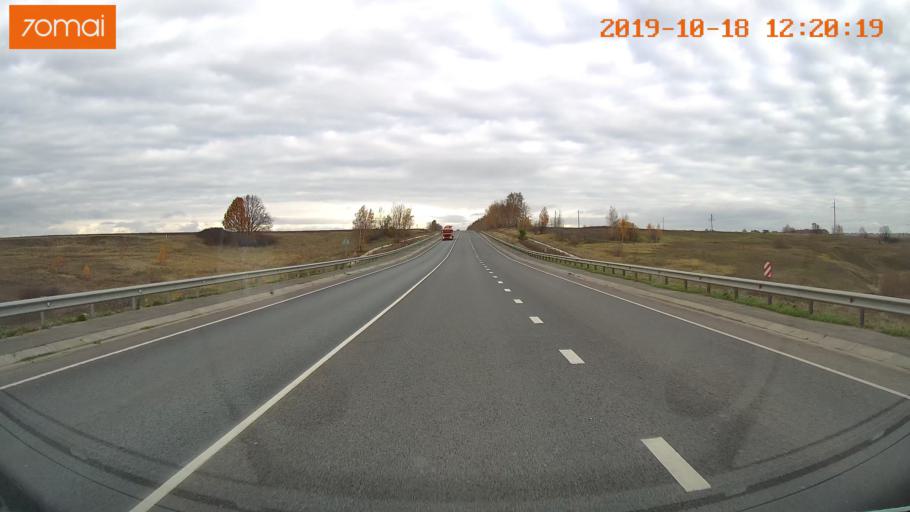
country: RU
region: Rjazan
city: Bagramovo
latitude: 54.4959
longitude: 39.4788
